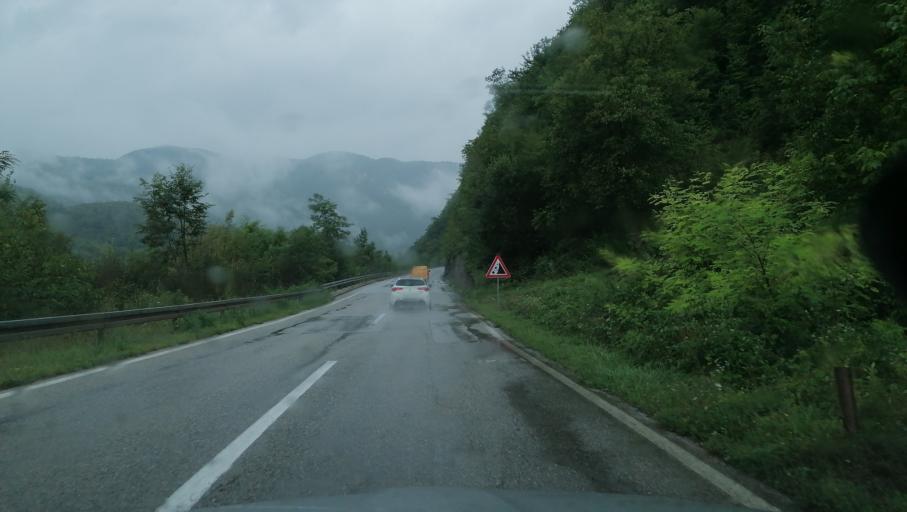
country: BA
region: Republika Srpska
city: Visegrad
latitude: 43.7116
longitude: 19.1691
